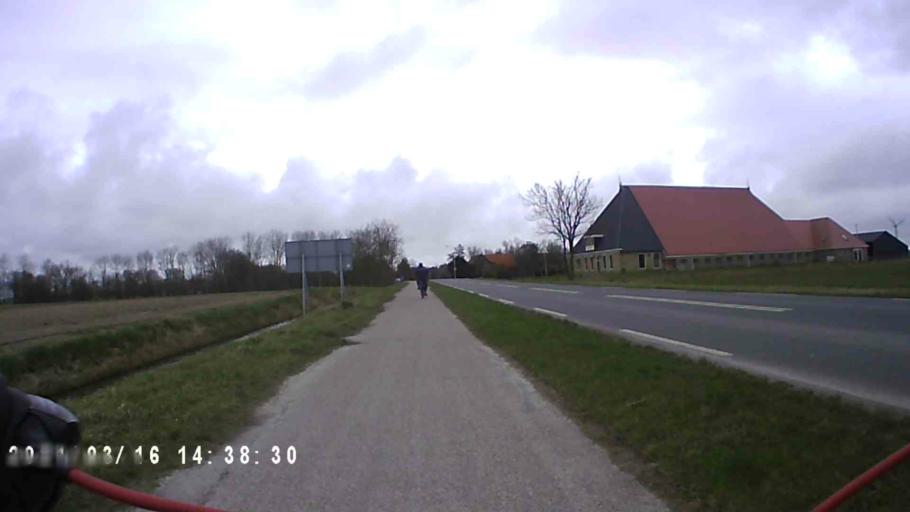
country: NL
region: Friesland
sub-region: Gemeente Harlingen
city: Harlingen
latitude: 53.1430
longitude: 5.4310
